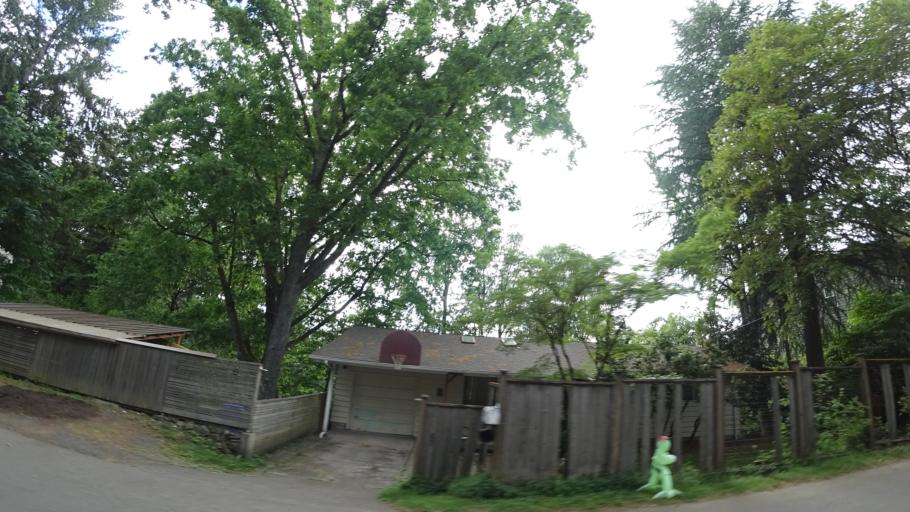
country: US
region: Oregon
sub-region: Washington County
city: Garden Home-Whitford
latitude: 45.4689
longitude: -122.7287
